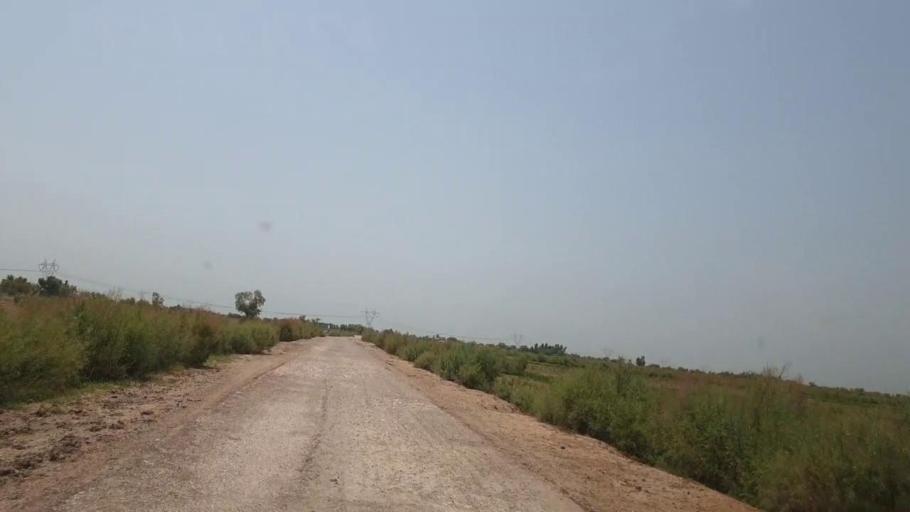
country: PK
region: Sindh
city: Shikarpur
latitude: 27.8955
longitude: 68.6315
